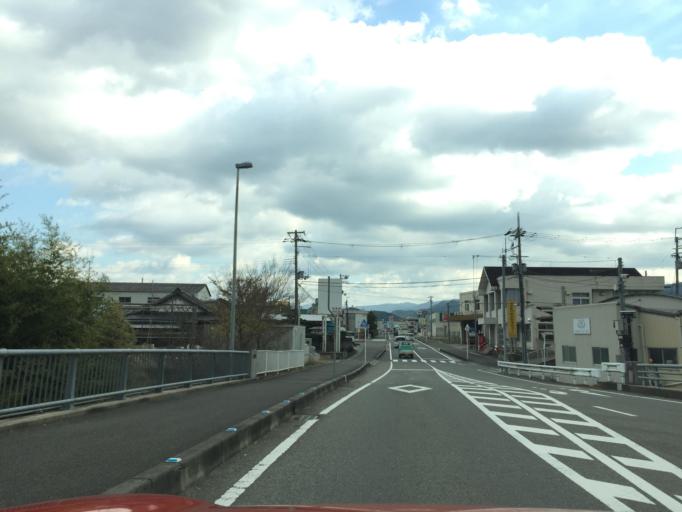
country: JP
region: Wakayama
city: Kainan
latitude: 34.1630
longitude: 135.2785
